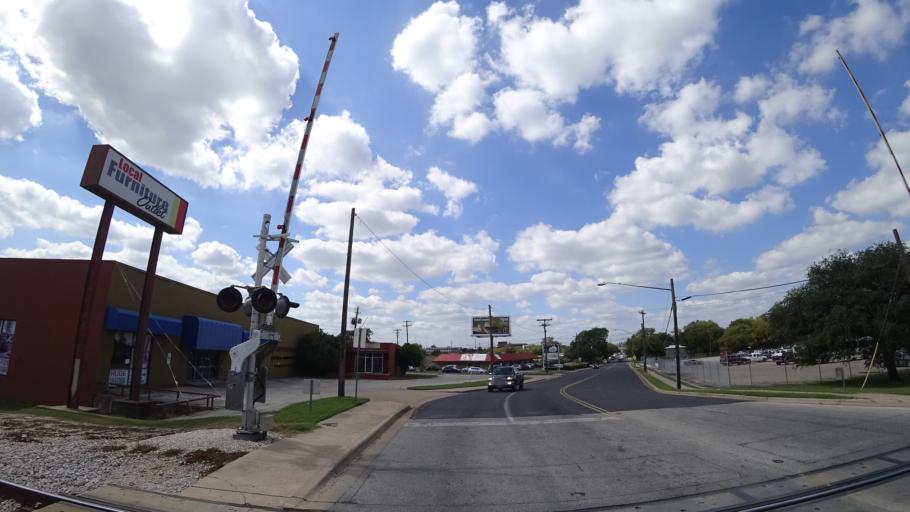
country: US
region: Texas
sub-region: Travis County
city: Austin
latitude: 30.3270
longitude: -97.7164
